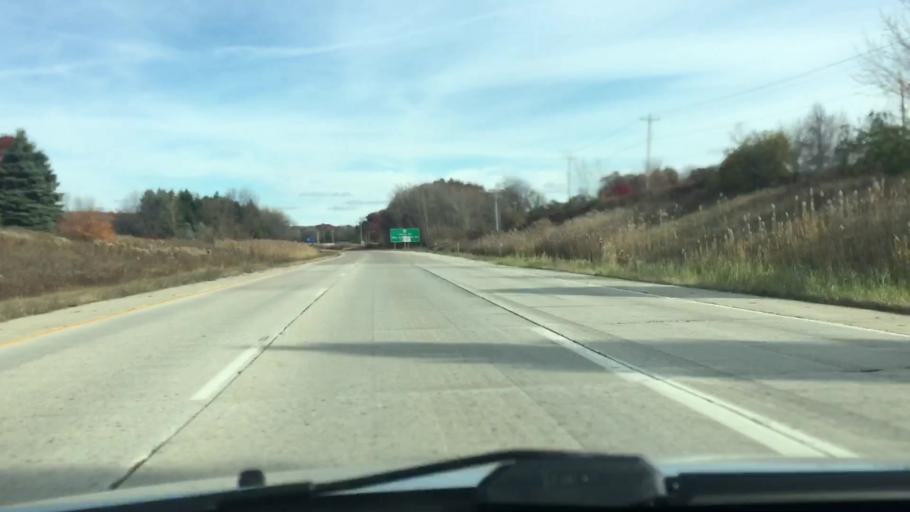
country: US
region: Wisconsin
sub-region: Brown County
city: Bellevue
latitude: 44.5247
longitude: -87.9316
